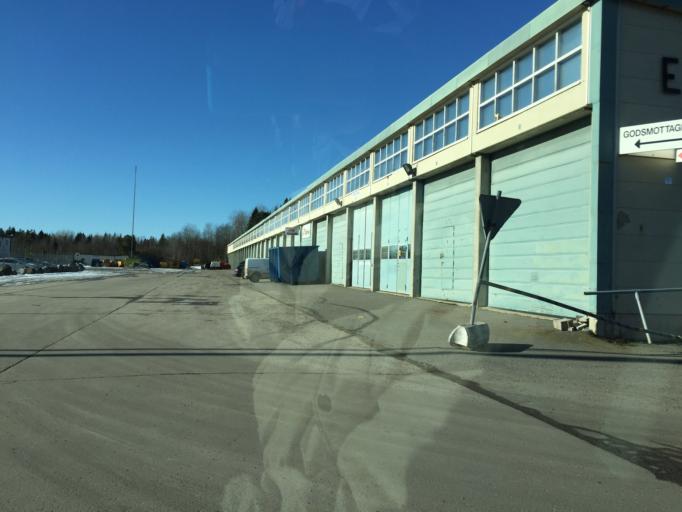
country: SE
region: Stockholm
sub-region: Nykvarns Kommun
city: Nykvarn
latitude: 59.1667
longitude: 17.5266
